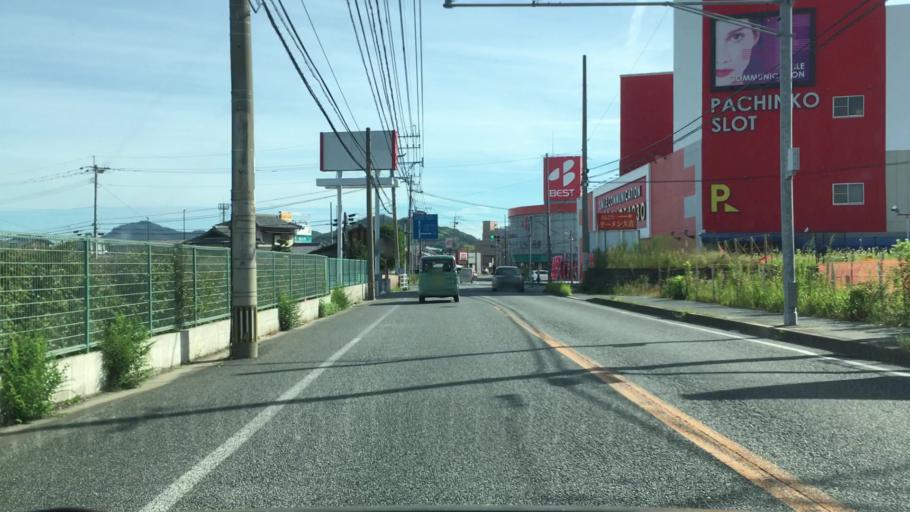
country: JP
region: Fukuoka
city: Maebaru-chuo
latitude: 33.5781
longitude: 130.2534
